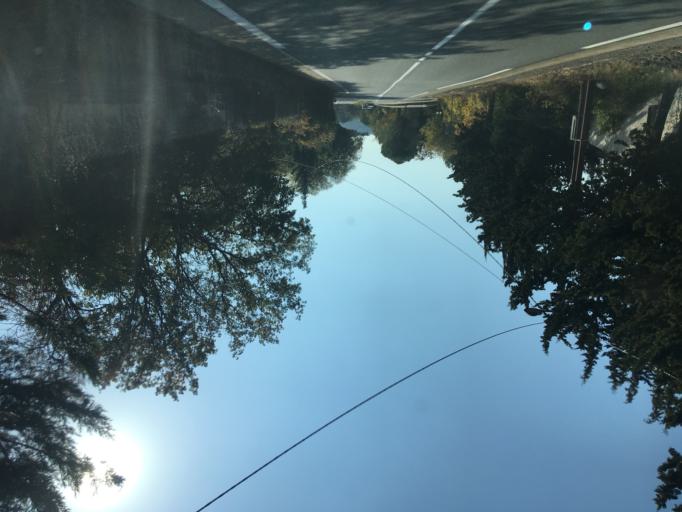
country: FR
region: Provence-Alpes-Cote d'Azur
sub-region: Departement du Var
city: Figanieres
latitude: 43.5675
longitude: 6.5069
